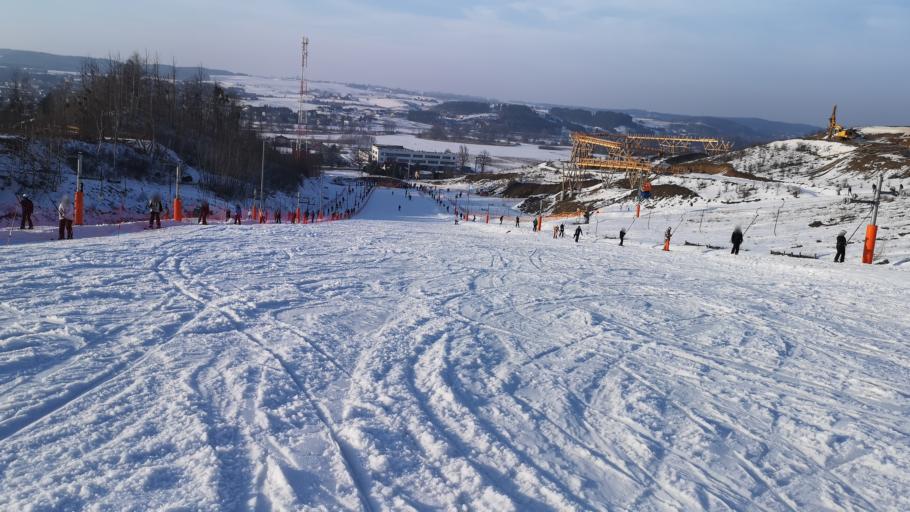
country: PL
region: Warmian-Masurian Voivodeship
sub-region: Powiat nowomiejski
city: Kurzetnik
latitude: 53.3979
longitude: 19.5882
